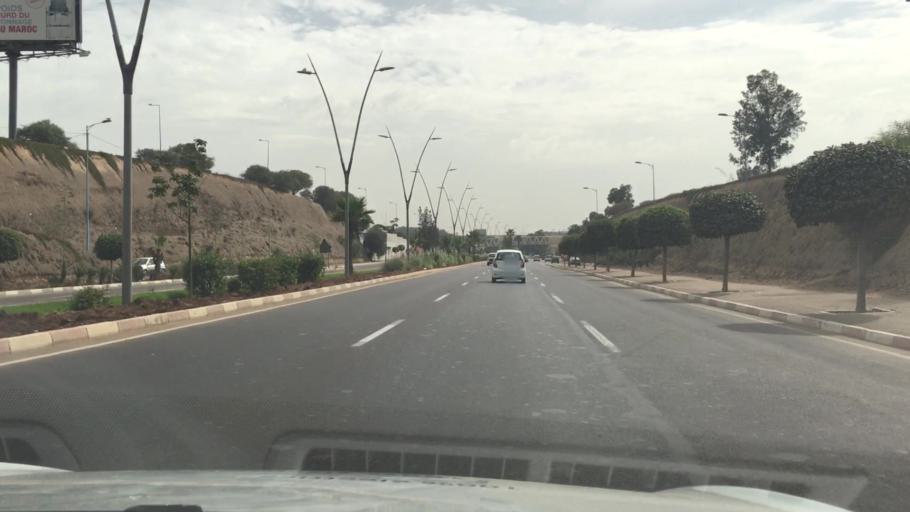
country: MA
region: Grand Casablanca
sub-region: Nouaceur
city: Bouskoura
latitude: 33.5183
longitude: -7.6327
